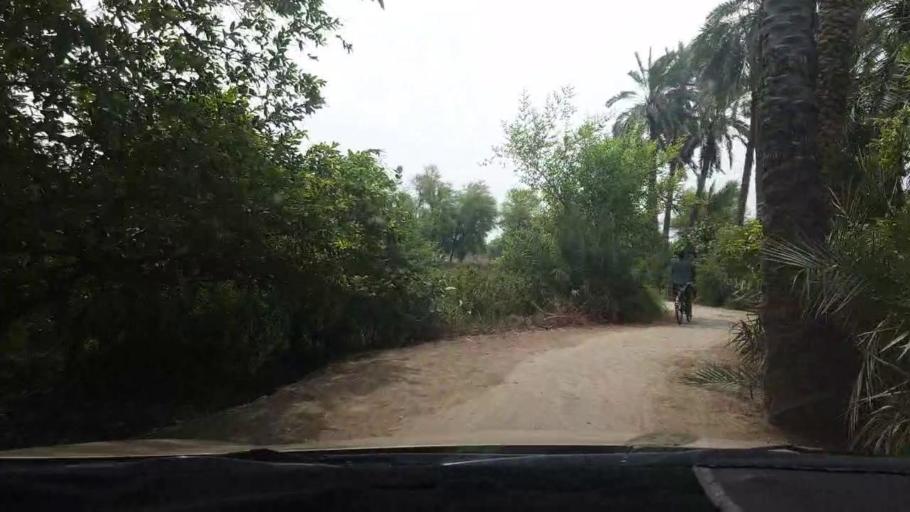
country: PK
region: Sindh
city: Naudero
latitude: 27.6284
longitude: 68.3105
